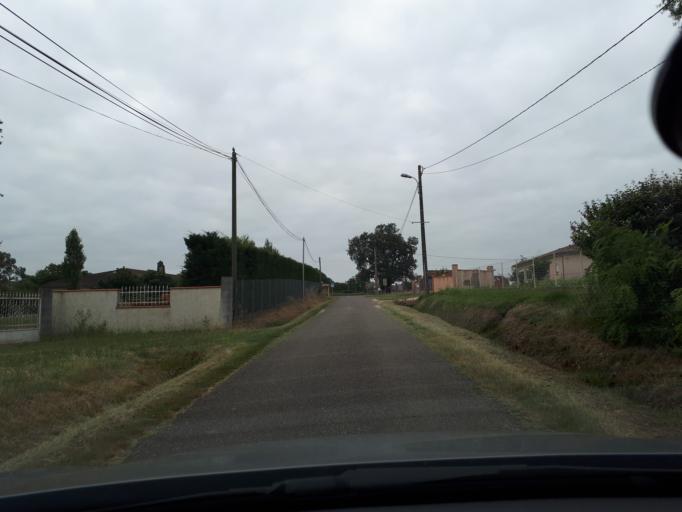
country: FR
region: Midi-Pyrenees
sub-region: Departement du Tarn-et-Garonne
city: Campsas
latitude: 43.8613
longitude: 1.3432
